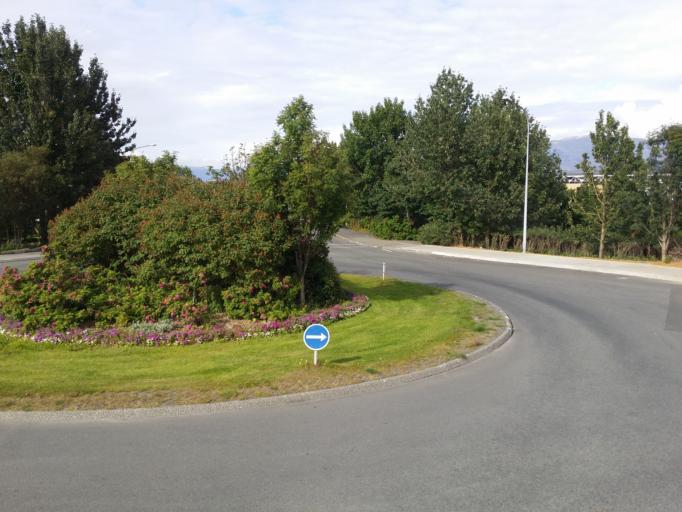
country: IS
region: Capital Region
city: Reykjavik
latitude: 64.1414
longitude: -21.8833
